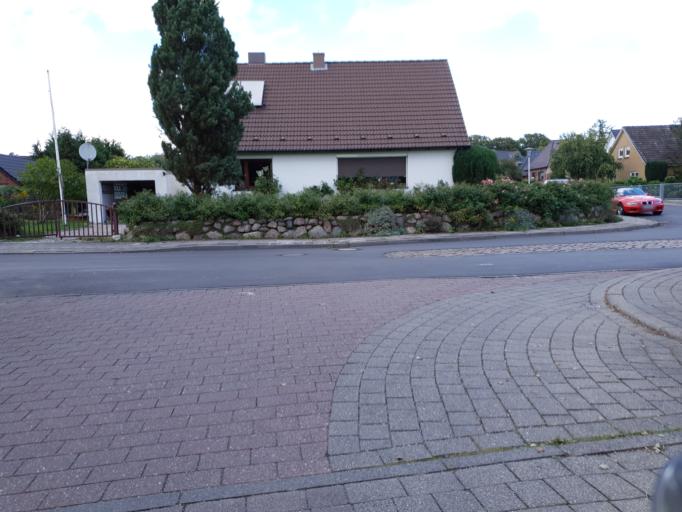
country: DE
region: Schleswig-Holstein
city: Kronshagen
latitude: 54.3310
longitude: 10.0955
